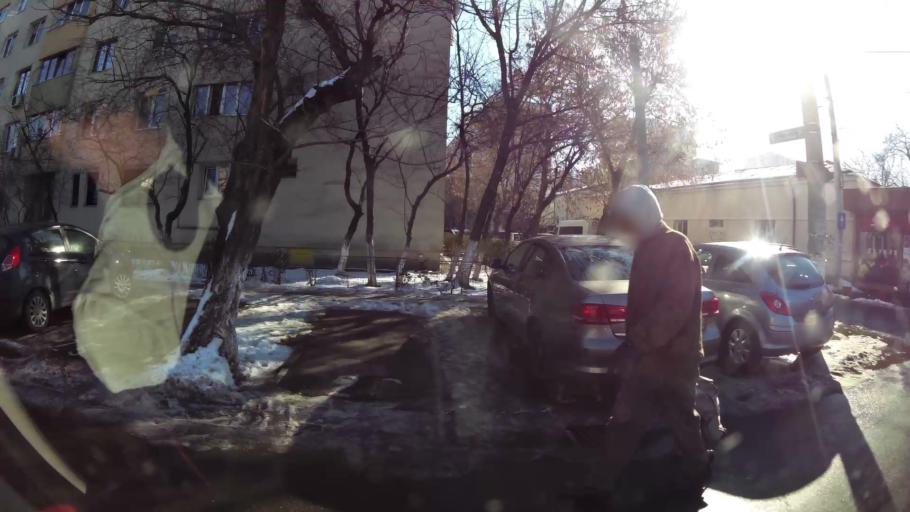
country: RO
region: Bucuresti
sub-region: Municipiul Bucuresti
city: Bucharest
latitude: 44.4616
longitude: 26.1244
